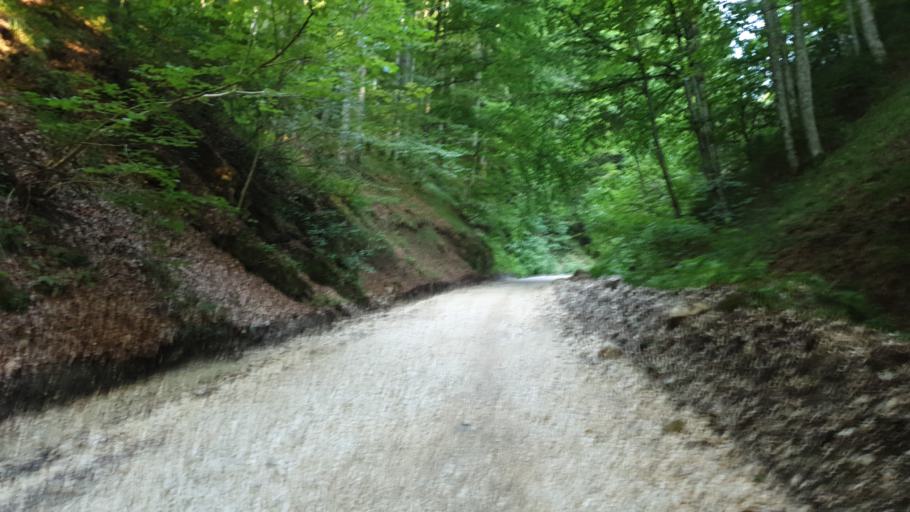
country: RO
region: Brasov
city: Brasov
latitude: 45.6139
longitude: 25.5634
